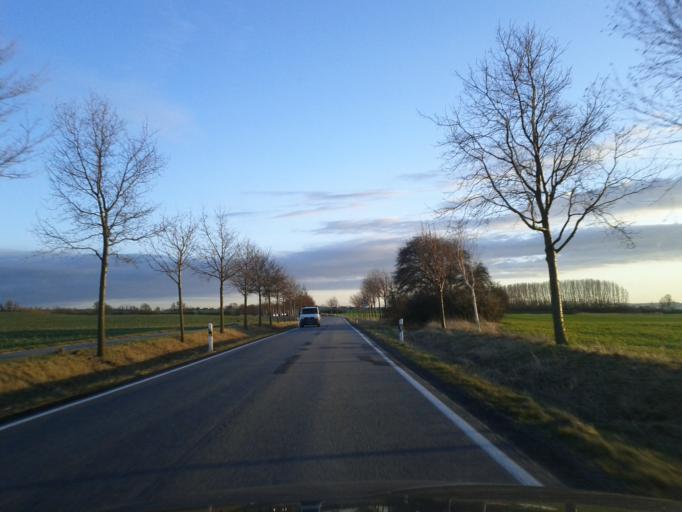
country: DE
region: Mecklenburg-Vorpommern
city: Blowatz
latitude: 53.9535
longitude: 11.4873
